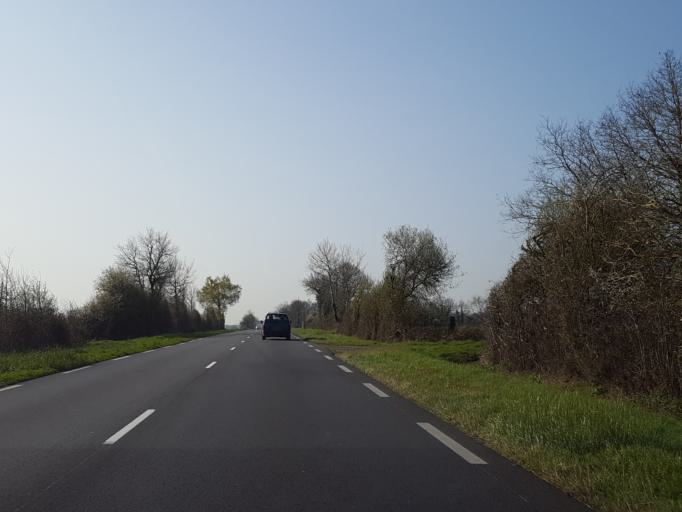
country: FR
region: Pays de la Loire
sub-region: Departement de la Loire-Atlantique
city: Geneston
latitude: 47.0318
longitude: -1.5062
